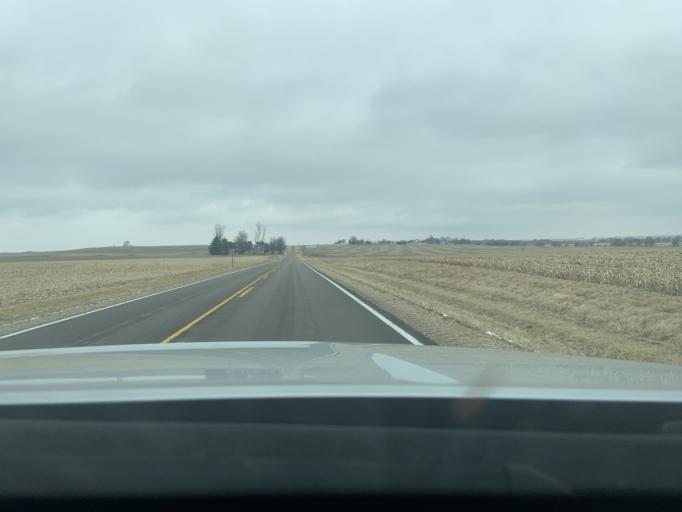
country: US
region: Illinois
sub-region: LaSalle County
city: Sheridan
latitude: 41.4615
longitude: -88.6155
